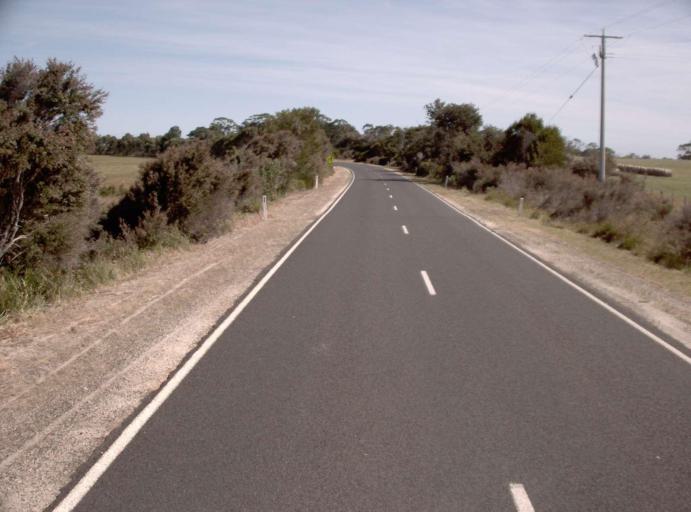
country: AU
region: Victoria
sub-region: Wellington
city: Sale
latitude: -38.3517
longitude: 147.1714
